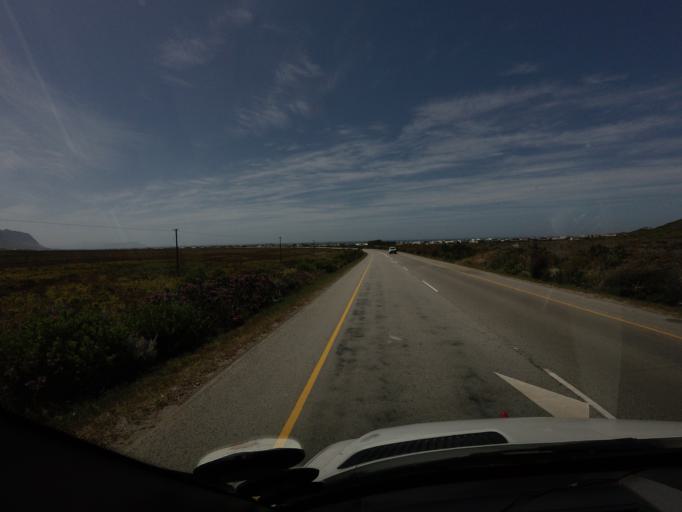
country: ZA
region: Western Cape
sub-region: Overberg District Municipality
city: Grabouw
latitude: -34.3586
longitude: 18.8631
